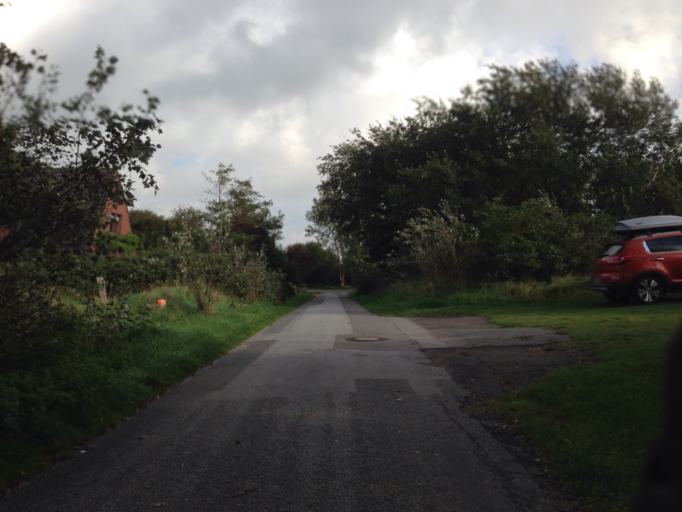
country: DE
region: Schleswig-Holstein
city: Utersum
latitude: 54.7037
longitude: 8.4159
